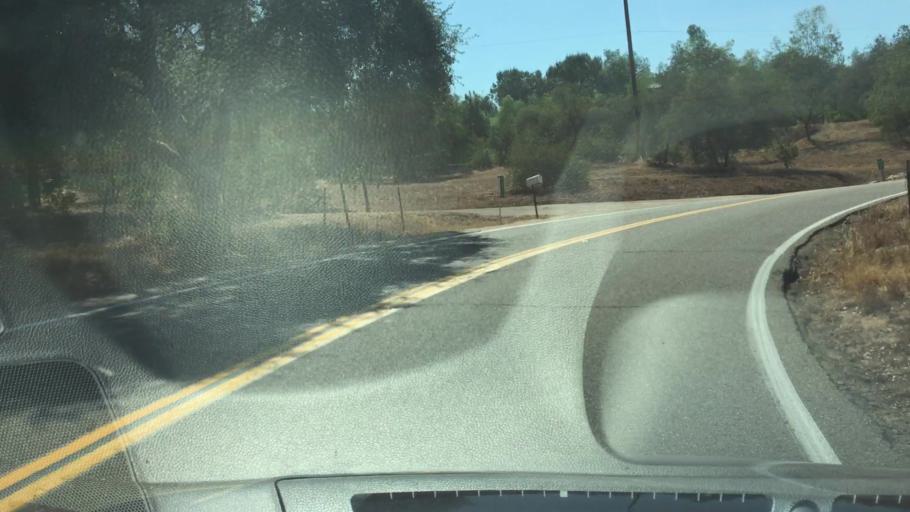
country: US
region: California
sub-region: San Diego County
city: Harbison Canyon
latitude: 32.7478
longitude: -116.7910
